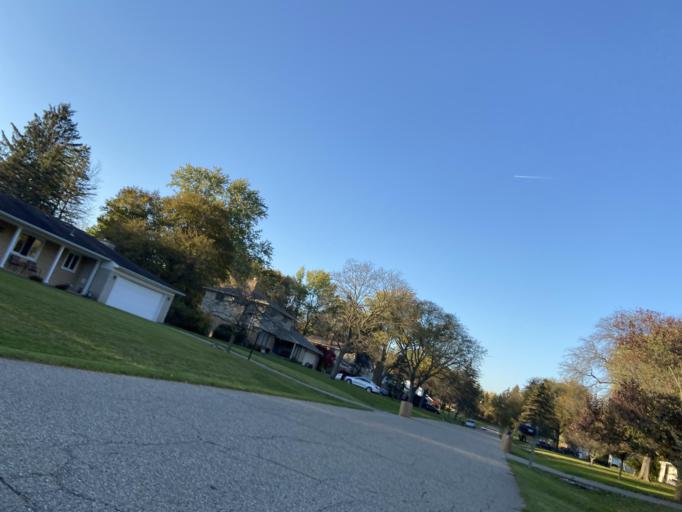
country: US
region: Michigan
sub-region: Oakland County
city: Franklin
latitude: 42.5337
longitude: -83.3352
